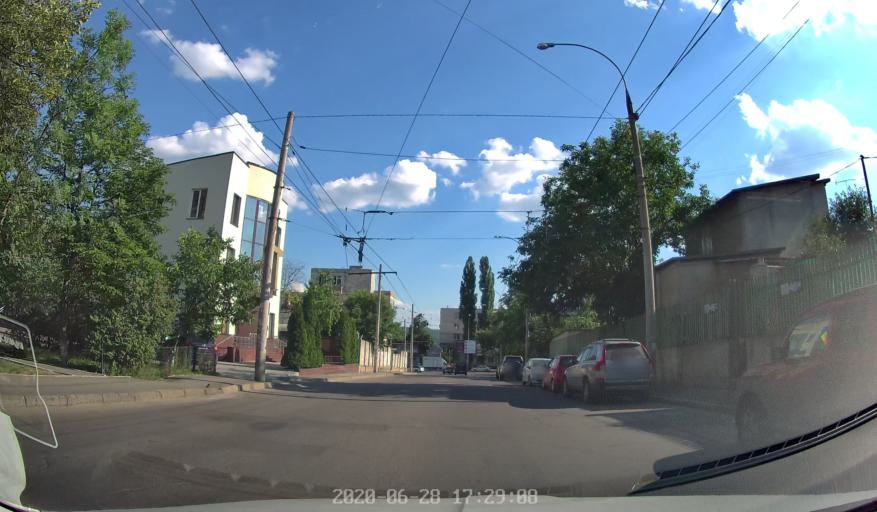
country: MD
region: Chisinau
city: Chisinau
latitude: 47.0242
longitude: 28.7925
